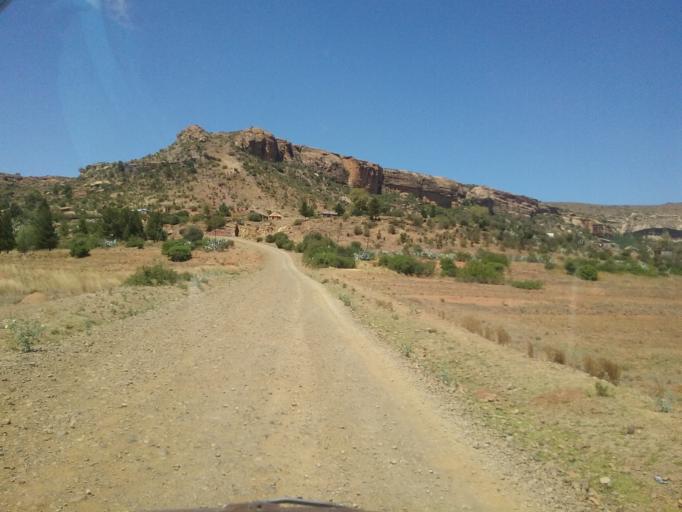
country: LS
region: Quthing
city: Quthing
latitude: -30.3050
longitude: 27.8109
